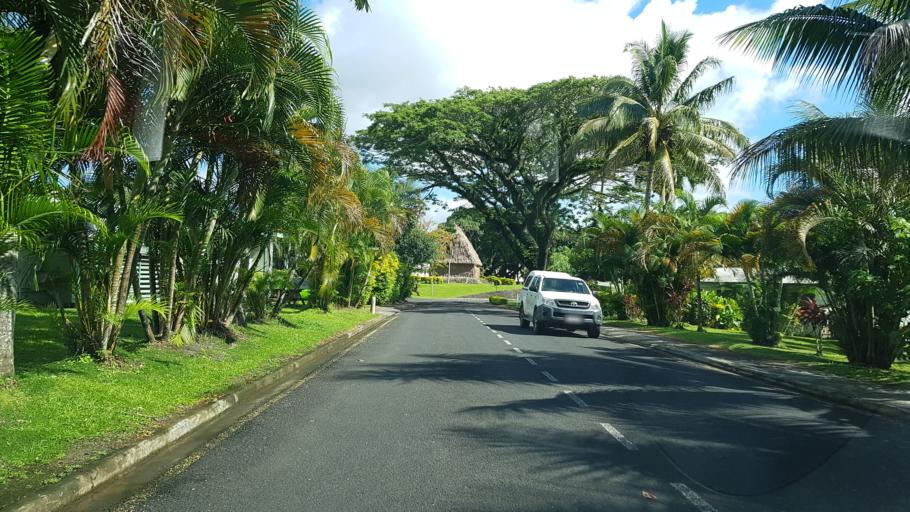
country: FJ
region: Central
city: Suva
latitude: -18.1525
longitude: 178.4437
